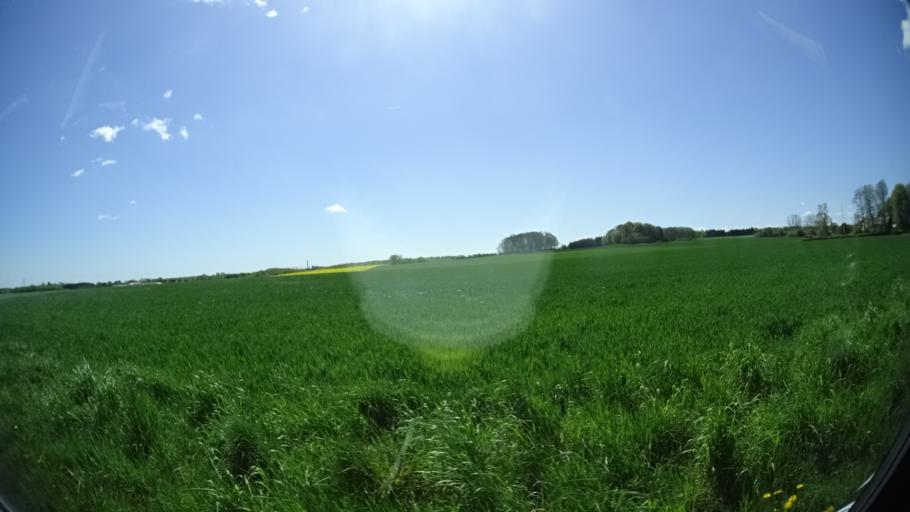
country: DK
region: Central Jutland
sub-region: Skanderborg Kommune
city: Horning
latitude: 56.1150
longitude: 10.0237
